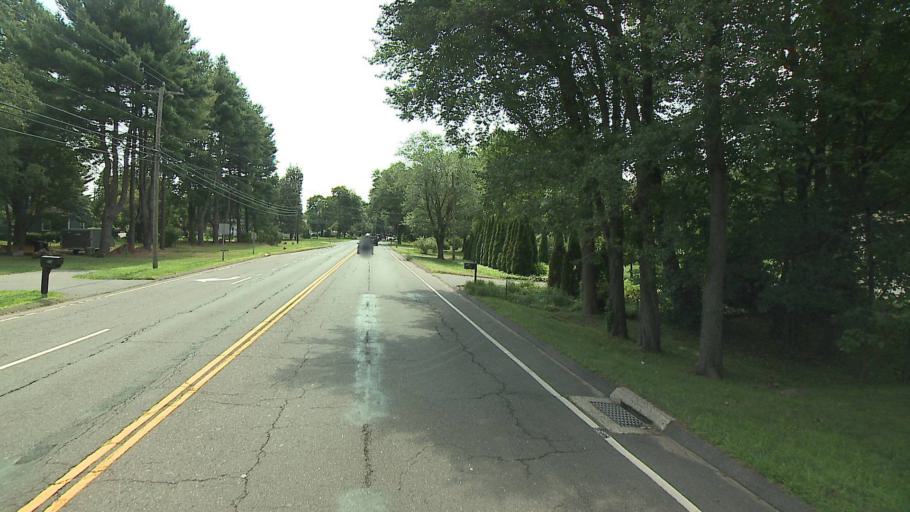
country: US
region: Connecticut
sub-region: Hartford County
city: Plainville
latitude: 41.7025
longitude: -72.8791
